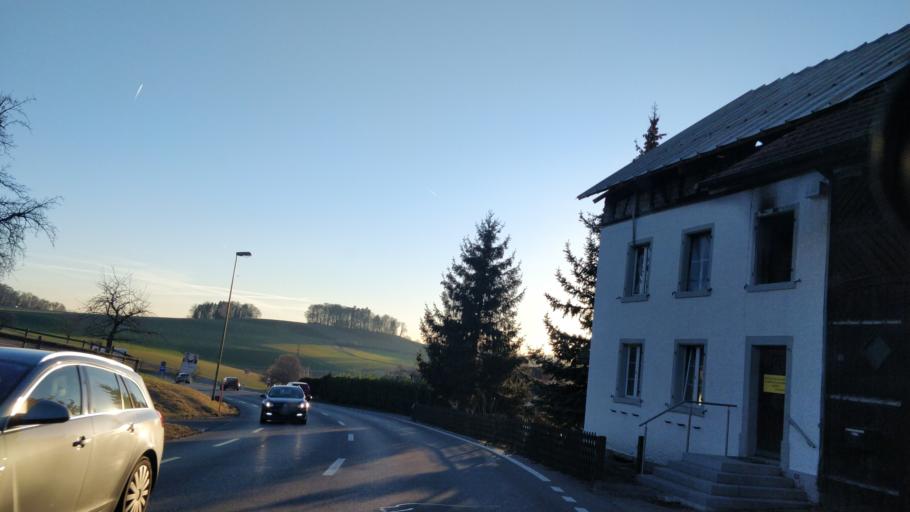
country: CH
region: Zurich
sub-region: Bezirk Buelach
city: Buelach / Gstueckt
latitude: 47.5164
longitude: 8.5643
